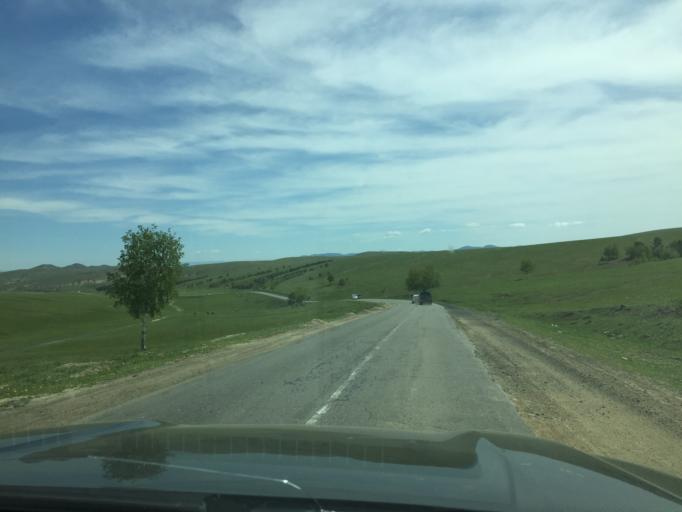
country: MN
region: Central Aimak
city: Javhlant
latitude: 48.6507
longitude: 106.0992
